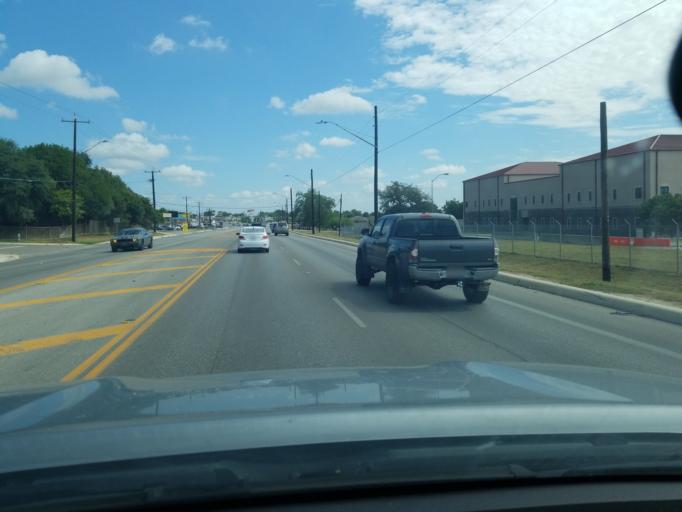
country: US
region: Texas
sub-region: Bexar County
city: Terrell Hills
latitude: 29.4812
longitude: -98.4320
